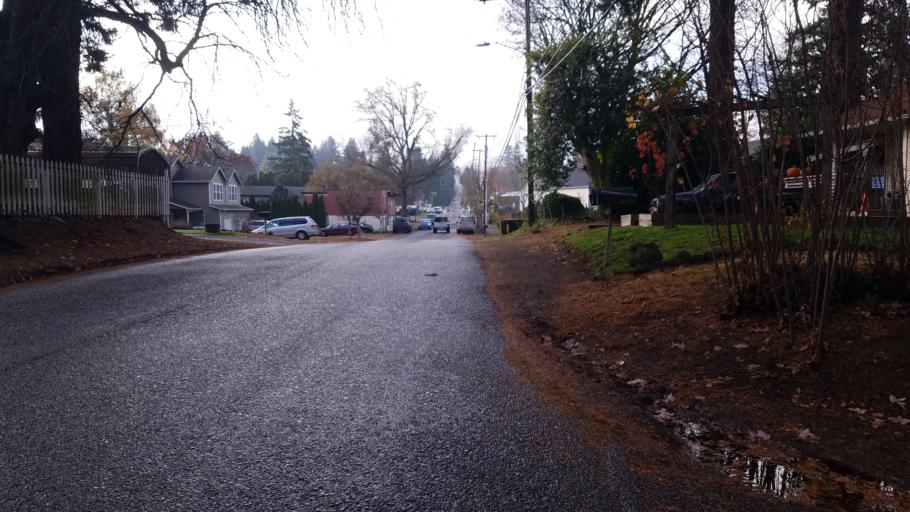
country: US
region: Oregon
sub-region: Clackamas County
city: Jennings Lodge
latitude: 45.3903
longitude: -122.6082
